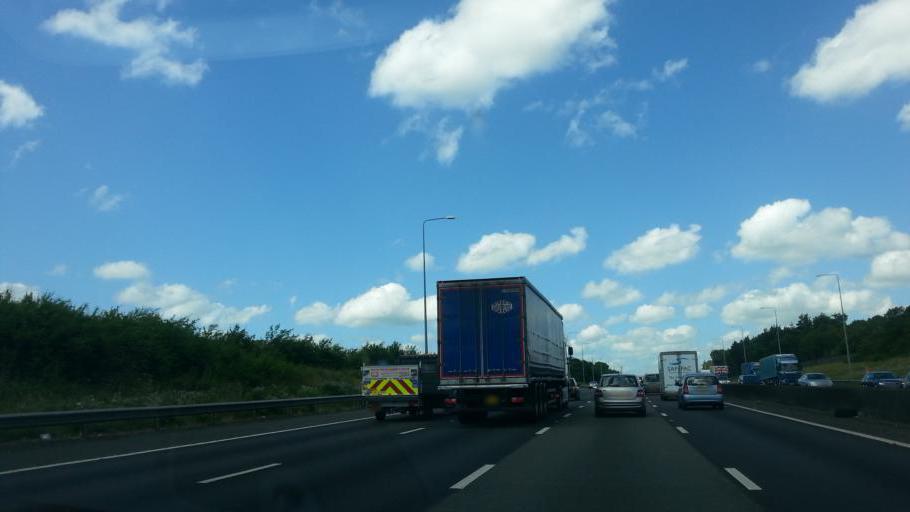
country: GB
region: England
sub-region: Buckinghamshire
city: Gerrards Cross
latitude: 51.5891
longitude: -0.5335
